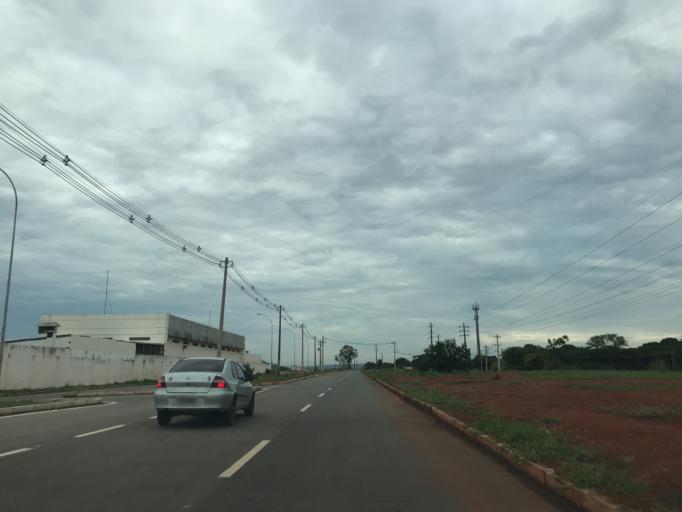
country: BR
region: Federal District
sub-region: Brasilia
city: Brasilia
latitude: -15.7779
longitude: -47.8950
